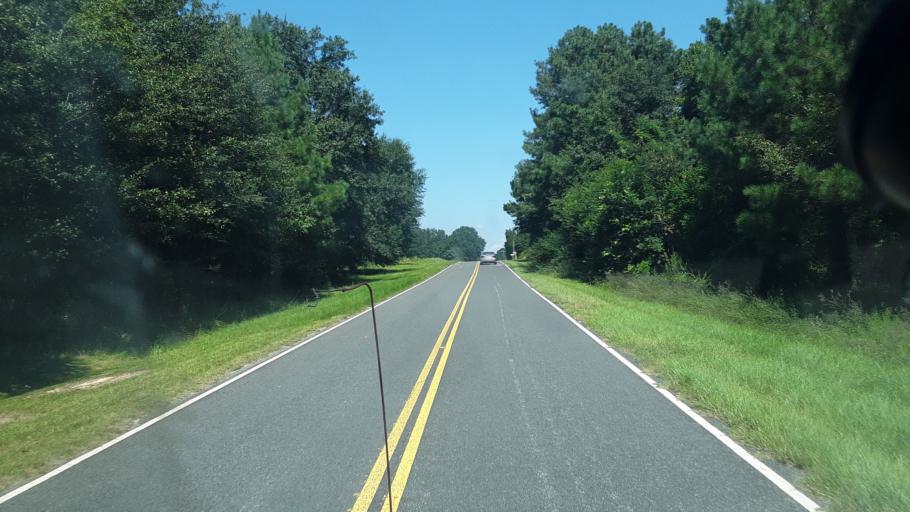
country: US
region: South Carolina
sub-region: Calhoun County
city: Oak Grove
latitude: 33.6254
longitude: -81.0137
